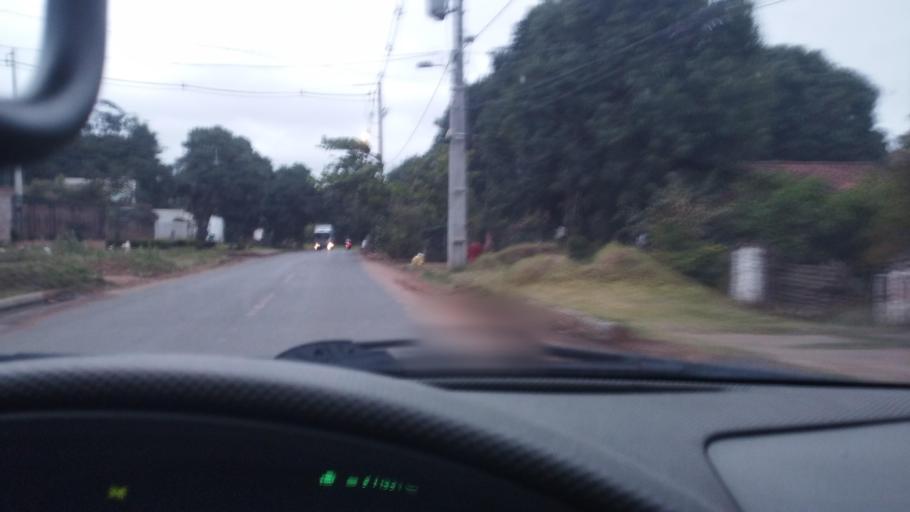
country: PY
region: Central
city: Fernando de la Mora
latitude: -25.2898
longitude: -57.5132
